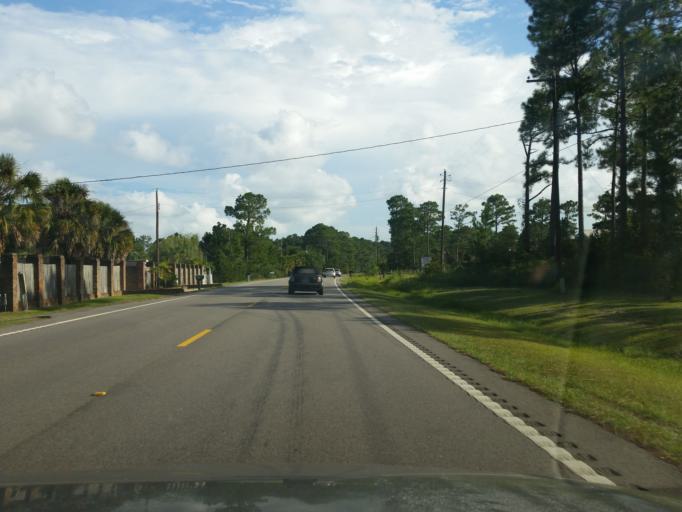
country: US
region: Alabama
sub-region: Mobile County
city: Dauphin Island
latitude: 30.3875
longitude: -88.1085
